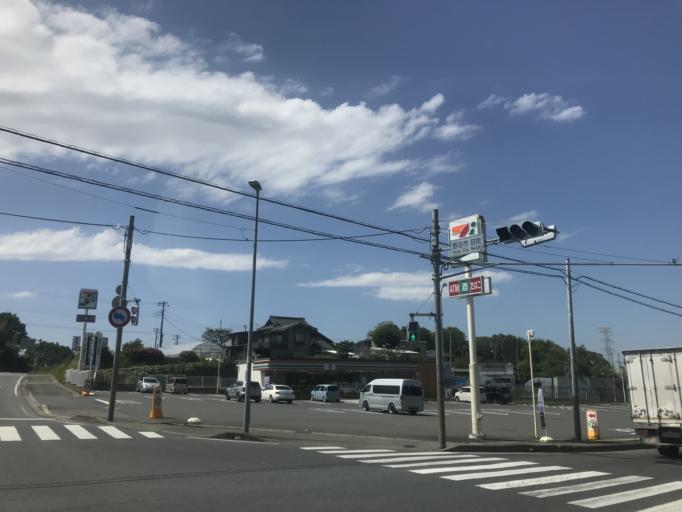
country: JP
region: Chiba
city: Noda
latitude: 35.9702
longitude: 139.8839
